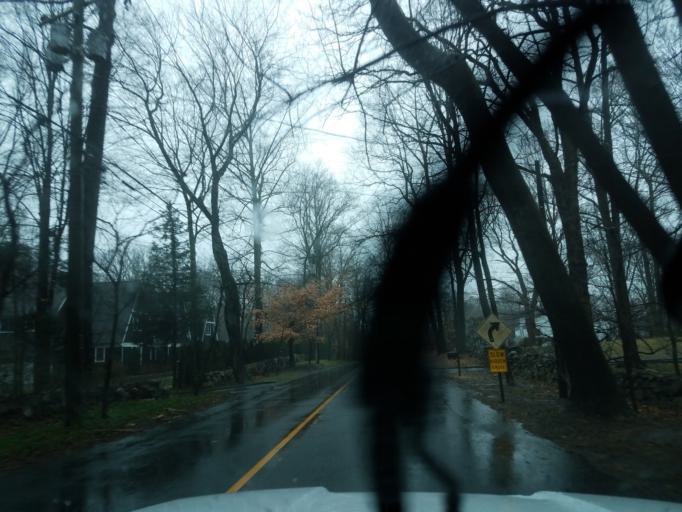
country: US
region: Connecticut
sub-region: Fairfield County
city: Darien
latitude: 41.0942
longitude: -73.5046
